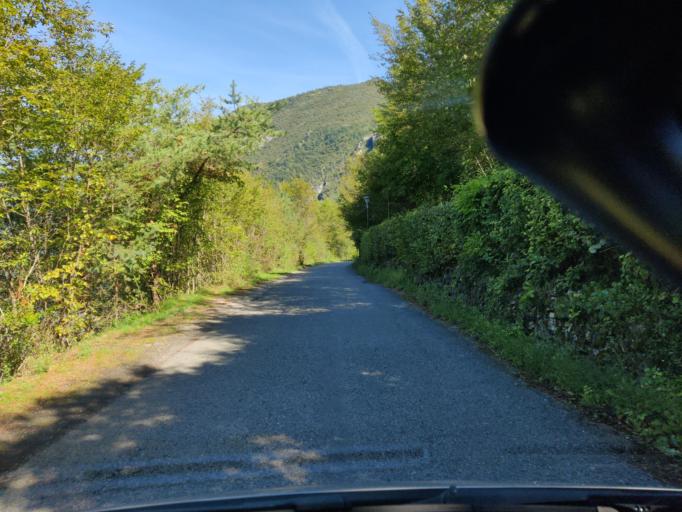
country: IT
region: Lombardy
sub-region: Provincia di Brescia
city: Anfo
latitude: 45.7693
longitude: 10.5190
